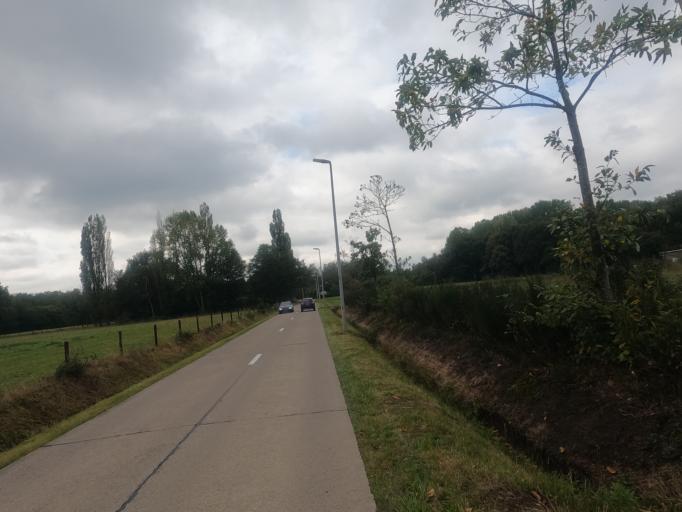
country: BE
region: Flanders
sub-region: Provincie Antwerpen
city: Nijlen
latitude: 51.1447
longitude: 4.6603
